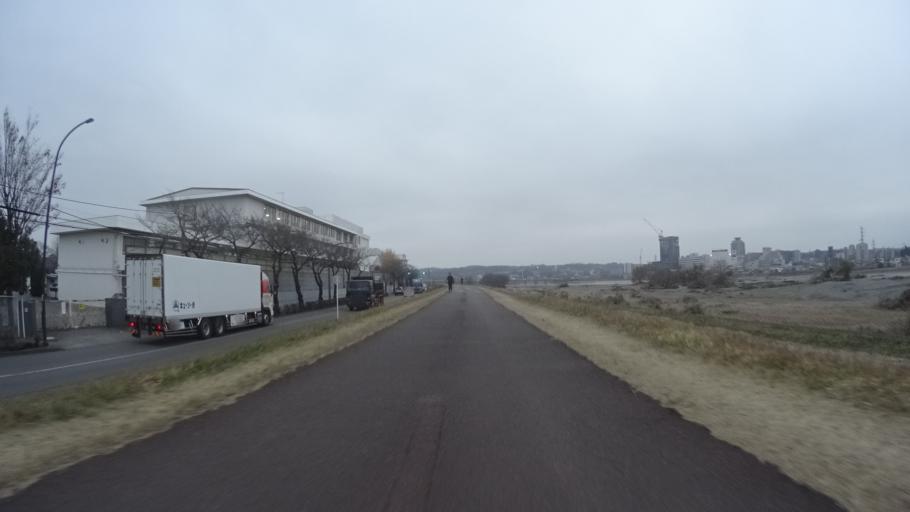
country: JP
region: Tokyo
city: Hino
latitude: 35.6594
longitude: 139.4437
